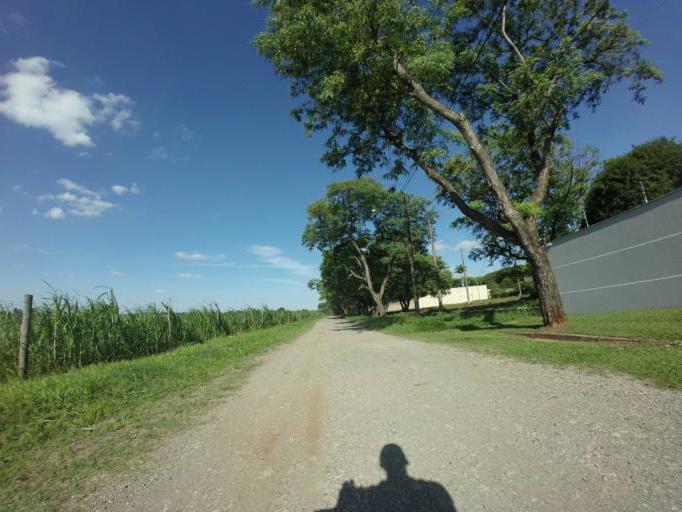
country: BR
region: Sao Paulo
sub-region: Piracicaba
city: Piracicaba
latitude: -22.7493
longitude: -47.5858
